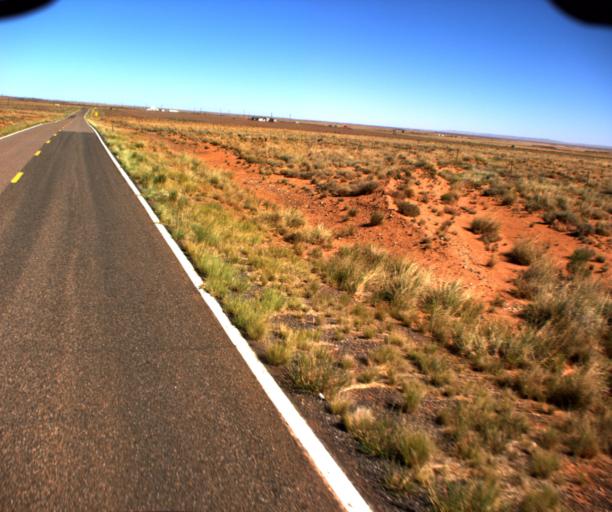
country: US
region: Arizona
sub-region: Coconino County
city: LeChee
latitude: 35.1325
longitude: -110.8821
